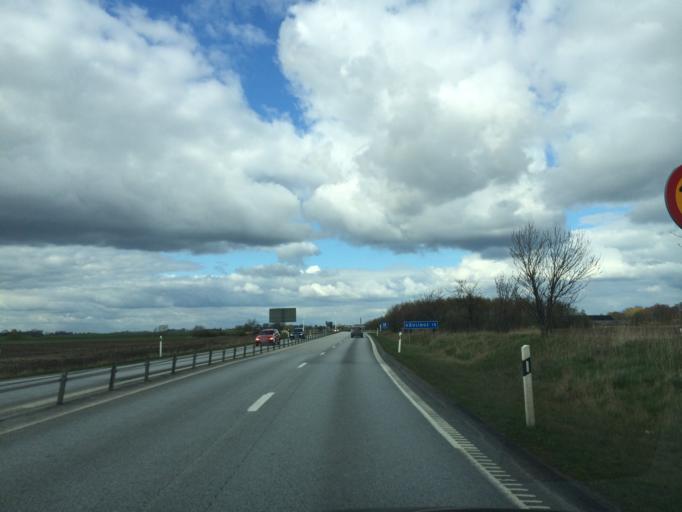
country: SE
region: Skane
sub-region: Staffanstorps Kommun
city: Hjaerup
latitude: 55.6970
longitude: 13.1345
